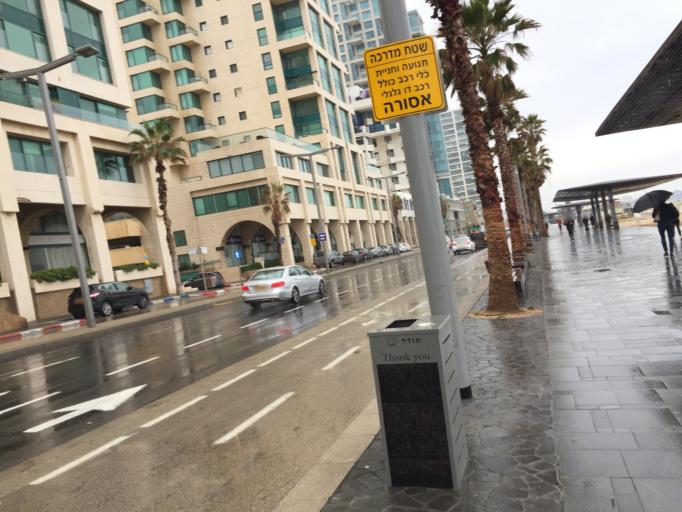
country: IL
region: Tel Aviv
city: Tel Aviv
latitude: 32.0722
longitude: 34.7644
